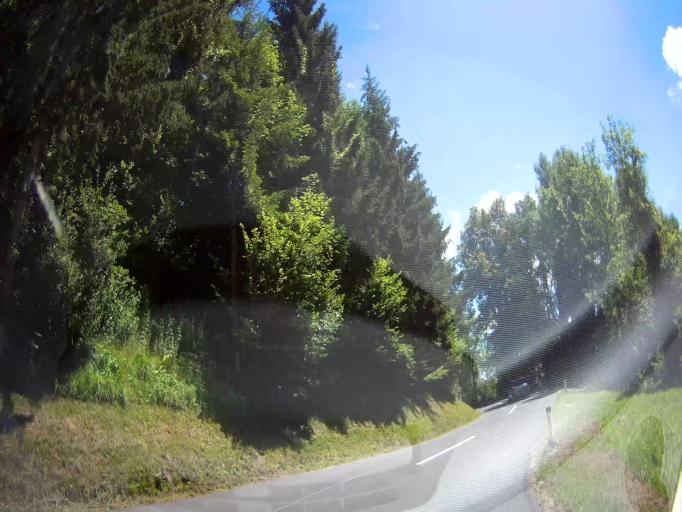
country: AT
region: Carinthia
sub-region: Politischer Bezirk Sankt Veit an der Glan
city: St. Georgen am Laengsee
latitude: 46.7225
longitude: 14.4310
